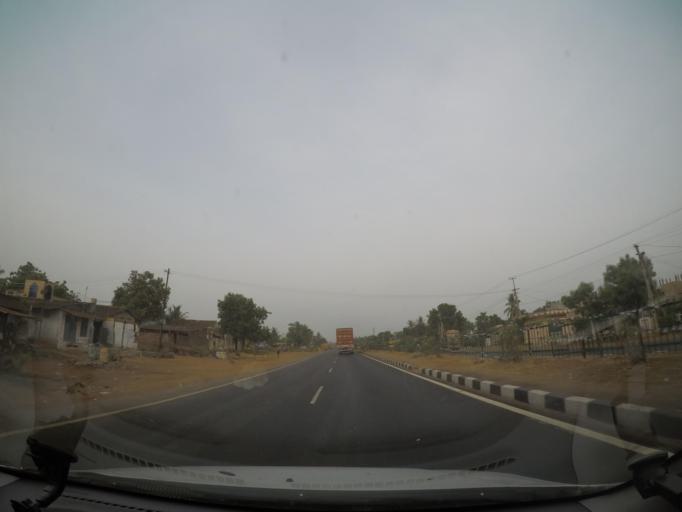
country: IN
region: Andhra Pradesh
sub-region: Krishna
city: Gannavaram
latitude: 16.6097
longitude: 80.9097
